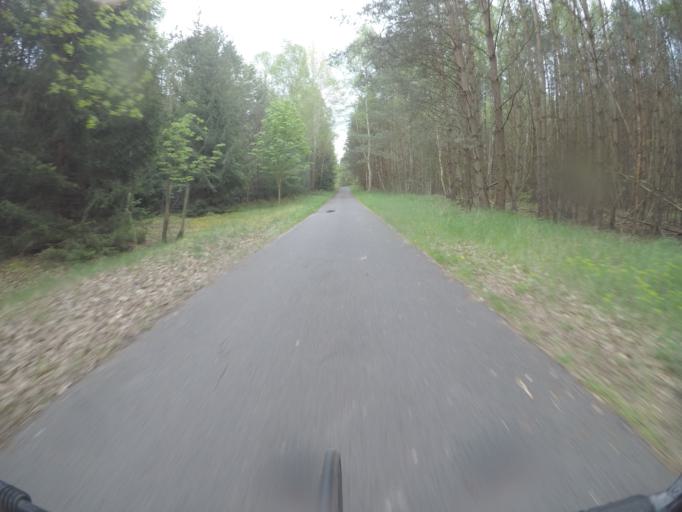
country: DE
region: Brandenburg
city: Biesenthal
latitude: 52.7954
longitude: 13.6270
